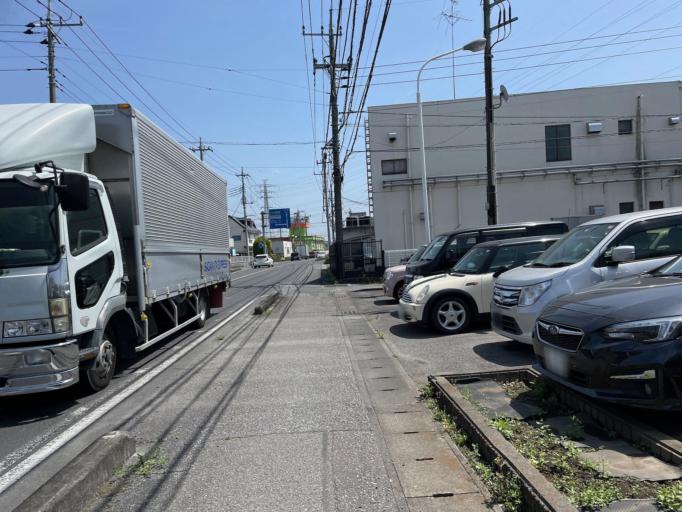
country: JP
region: Tochigi
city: Ashikaga
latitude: 36.3080
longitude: 139.4439
